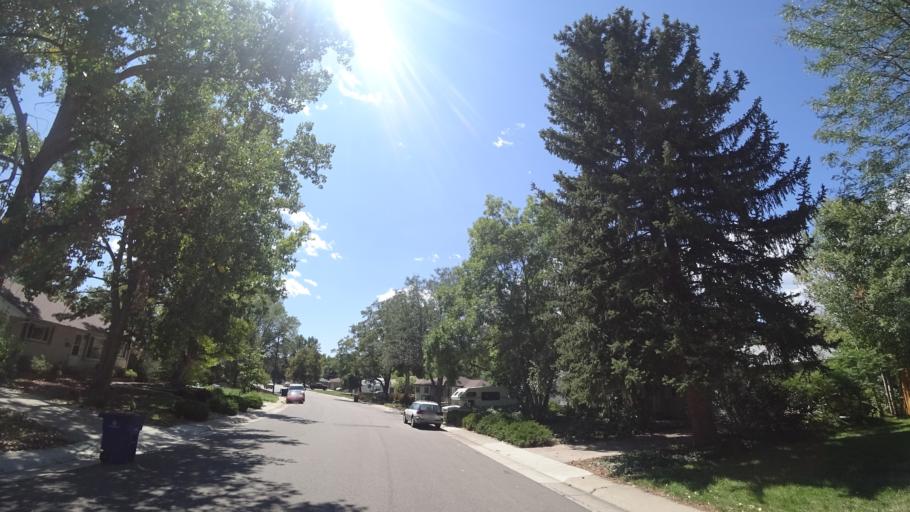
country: US
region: Colorado
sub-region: Arapahoe County
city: Littleton
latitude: 39.6113
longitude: -104.9970
